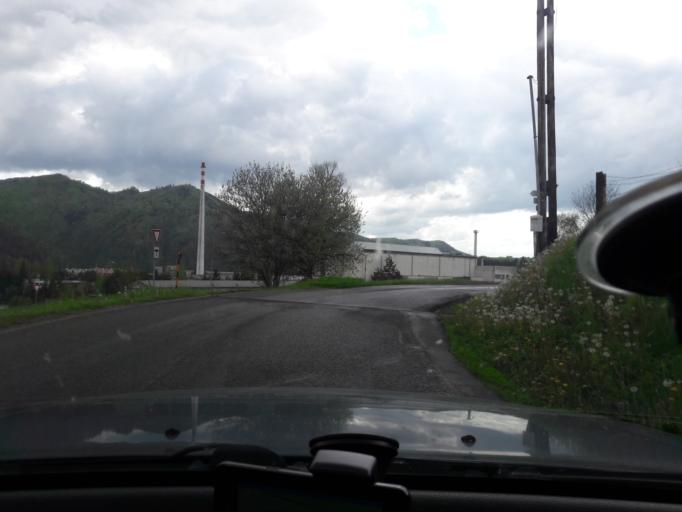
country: SK
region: Banskobystricky
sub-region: Okres Banska Bystrica
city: Brezno
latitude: 48.8134
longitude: 19.5676
